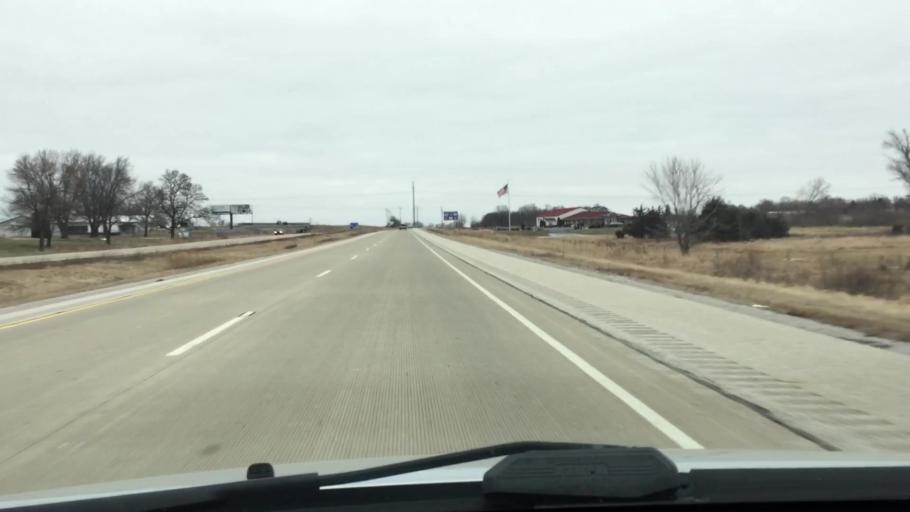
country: US
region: Wisconsin
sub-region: Jefferson County
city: Watertown
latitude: 43.1457
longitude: -88.7350
